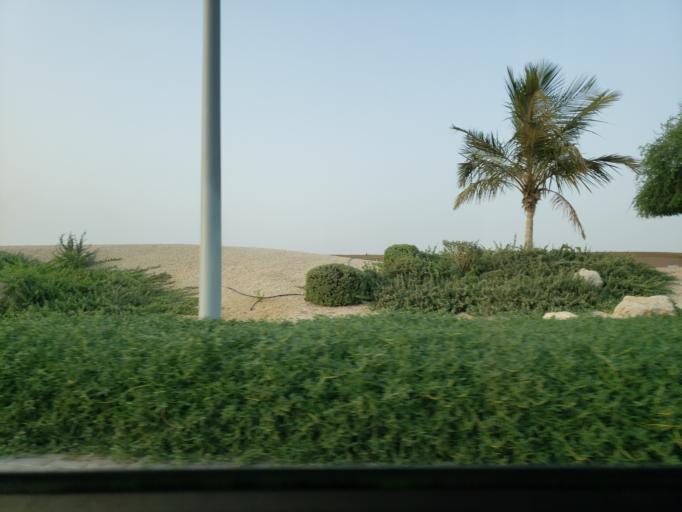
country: AE
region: Ajman
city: Ajman
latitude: 25.4358
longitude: 55.4806
